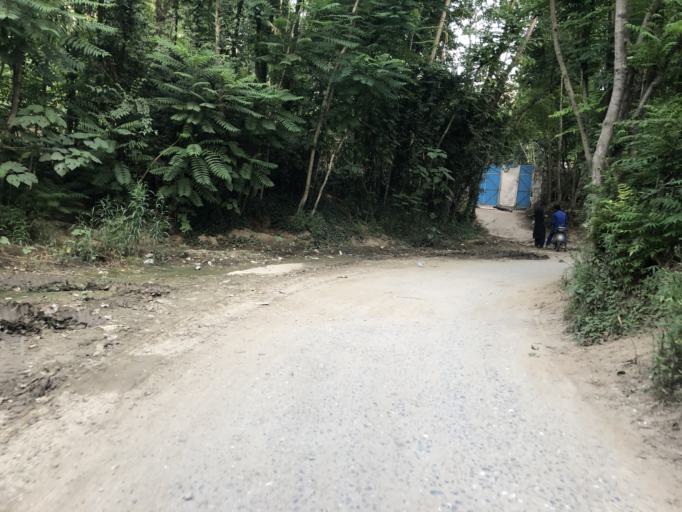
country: PK
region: Khyber Pakhtunkhwa
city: Daggar
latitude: 34.5797
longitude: 72.4551
